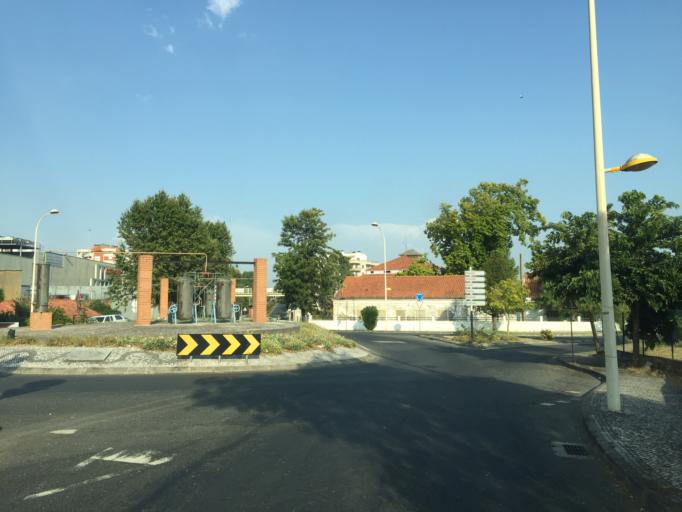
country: PT
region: Santarem
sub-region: Torres Novas
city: Torres Novas
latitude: 39.4726
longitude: -8.5478
